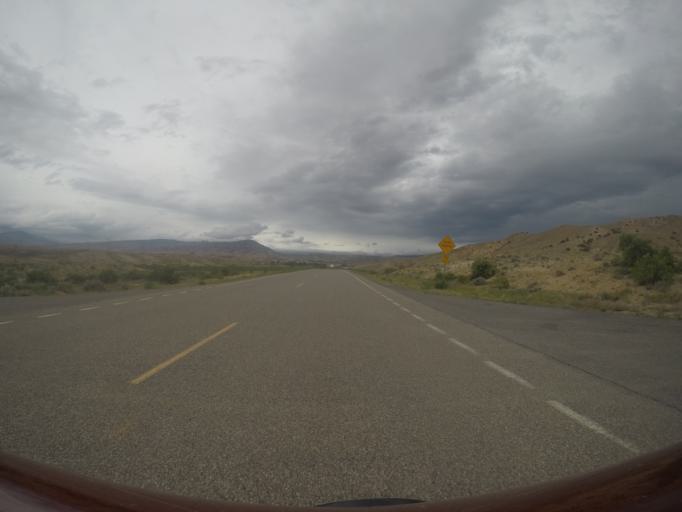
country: US
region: Wyoming
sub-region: Big Horn County
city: Lovell
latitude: 44.9512
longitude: -108.2960
